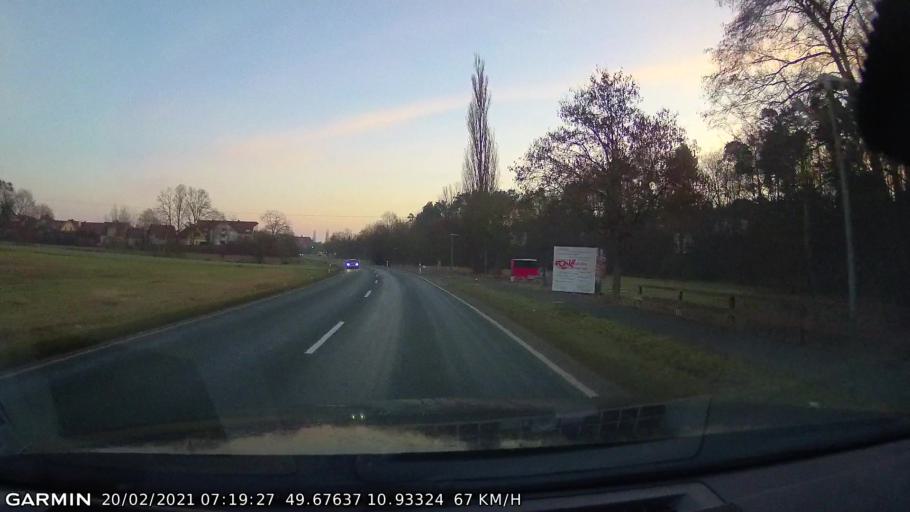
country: DE
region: Bavaria
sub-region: Regierungsbezirk Mittelfranken
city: Hemhofen
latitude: 49.6764
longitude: 10.9332
